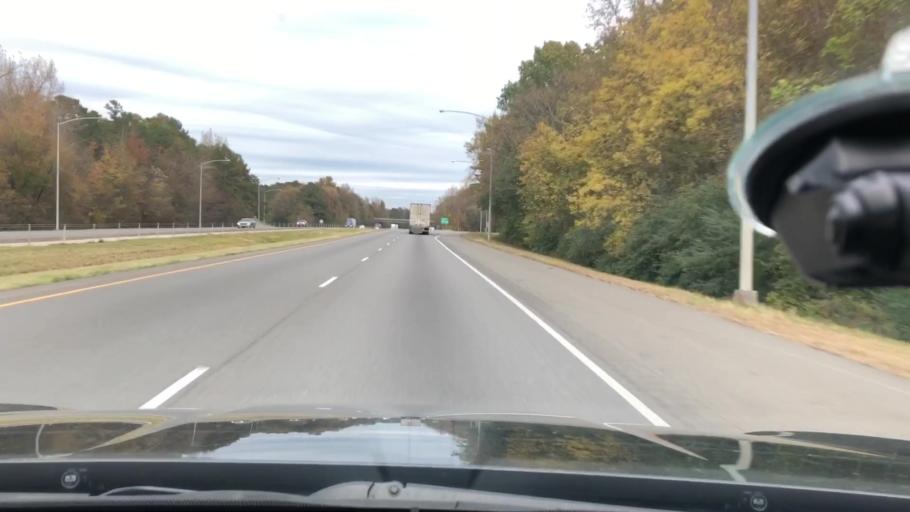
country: US
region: Arkansas
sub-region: Hot Spring County
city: Malvern
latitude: 34.3818
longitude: -92.8493
